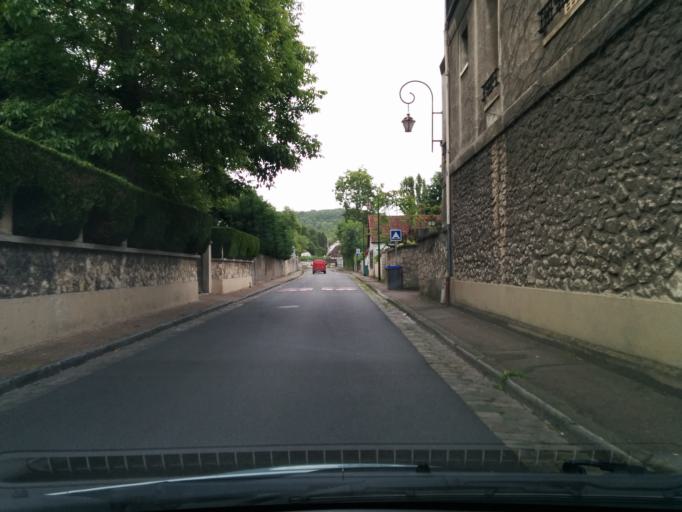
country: FR
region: Ile-de-France
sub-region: Departement des Yvelines
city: Follainville-Dennemont
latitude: 49.0111
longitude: 1.7015
